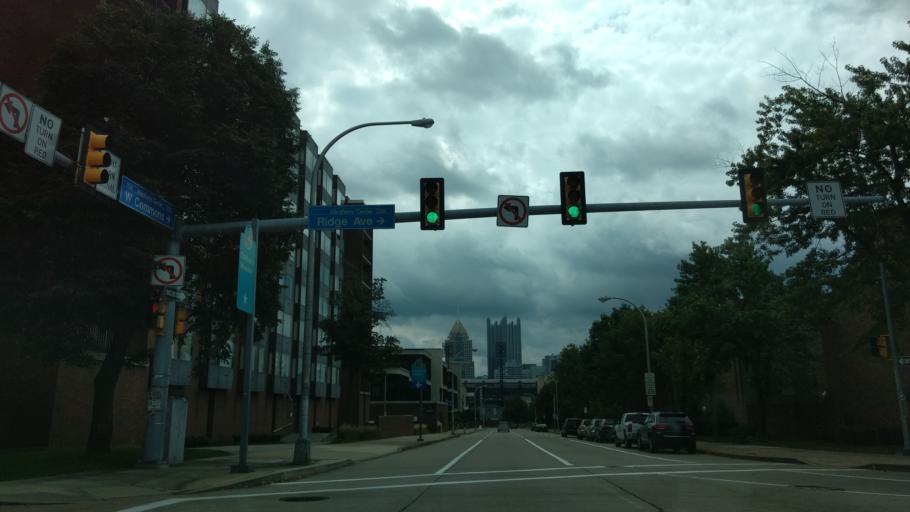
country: US
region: Pennsylvania
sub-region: Allegheny County
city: Pittsburgh
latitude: 40.4524
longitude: -80.0082
